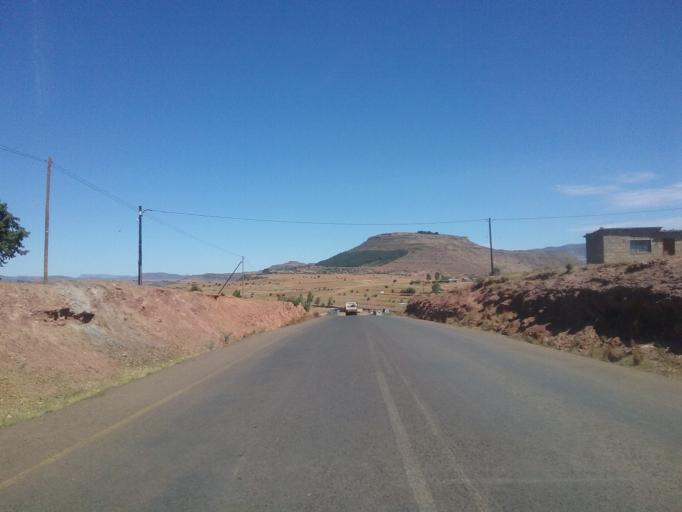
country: LS
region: Quthing
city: Quthing
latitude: -30.3909
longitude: 27.6270
